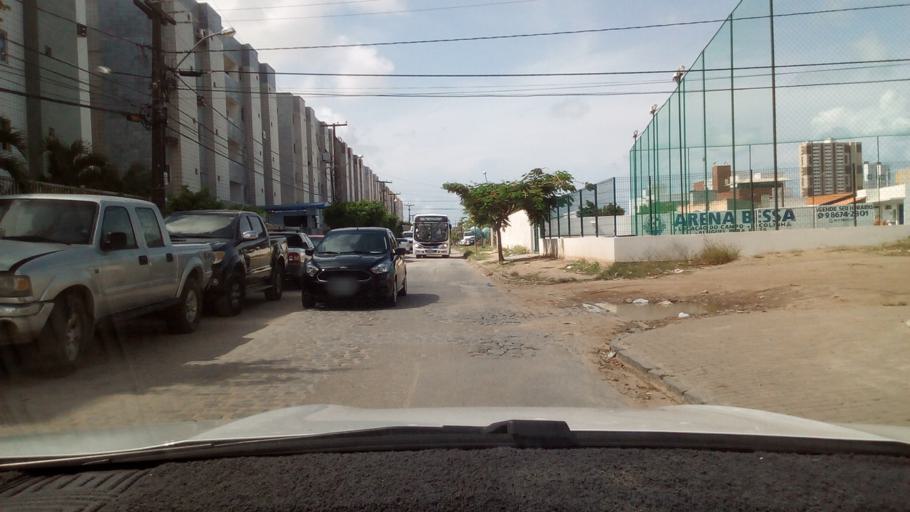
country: BR
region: Paraiba
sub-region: Joao Pessoa
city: Joao Pessoa
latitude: -7.0836
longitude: -34.8462
